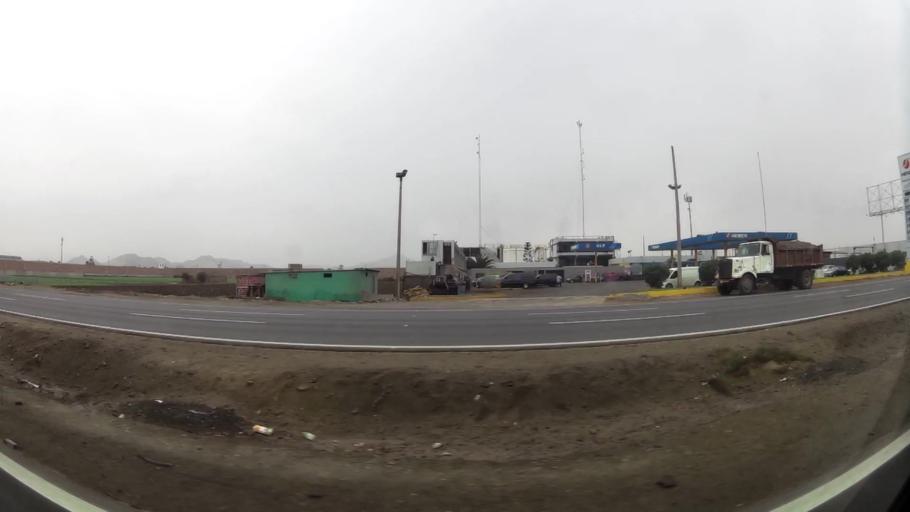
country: PE
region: Lima
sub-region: Lima
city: Punta Hermosa
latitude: -12.2926
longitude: -76.8636
